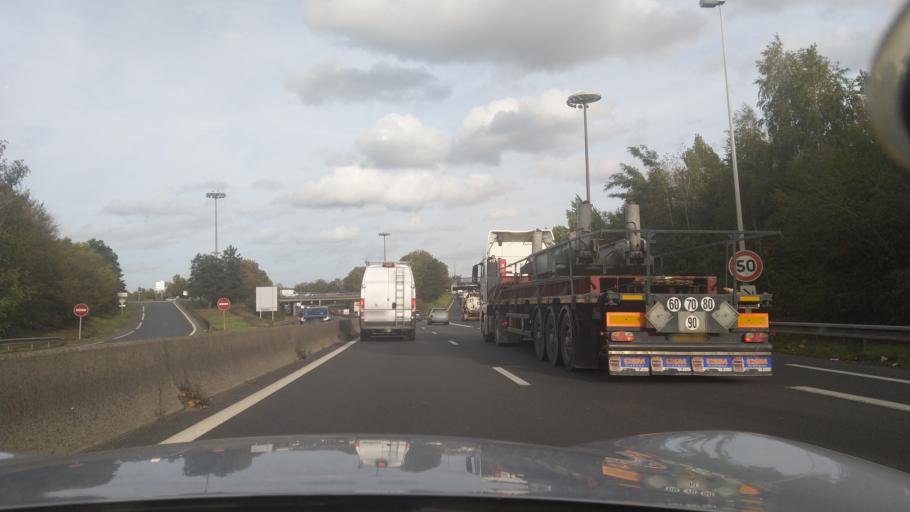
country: FR
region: Ile-de-France
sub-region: Departement du Val-d'Oise
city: Saint-Ouen-l'Aumone
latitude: 49.0357
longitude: 2.1182
